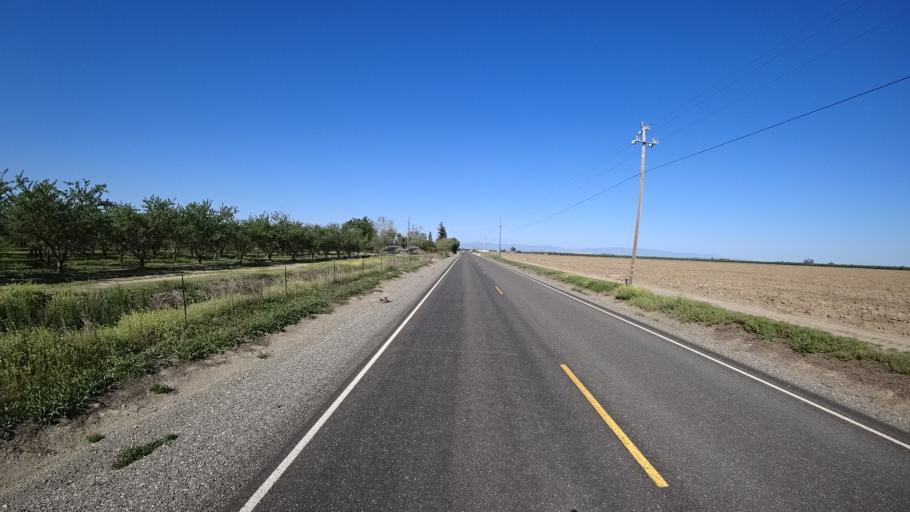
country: US
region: California
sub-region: Glenn County
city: Hamilton City
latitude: 39.7092
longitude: -122.0692
